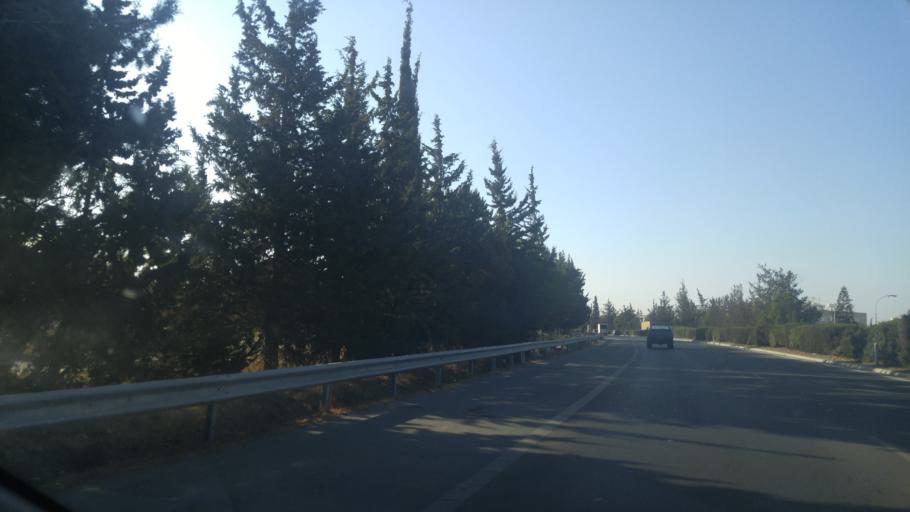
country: CY
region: Limassol
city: Pano Polemidia
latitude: 34.6852
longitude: 33.0079
